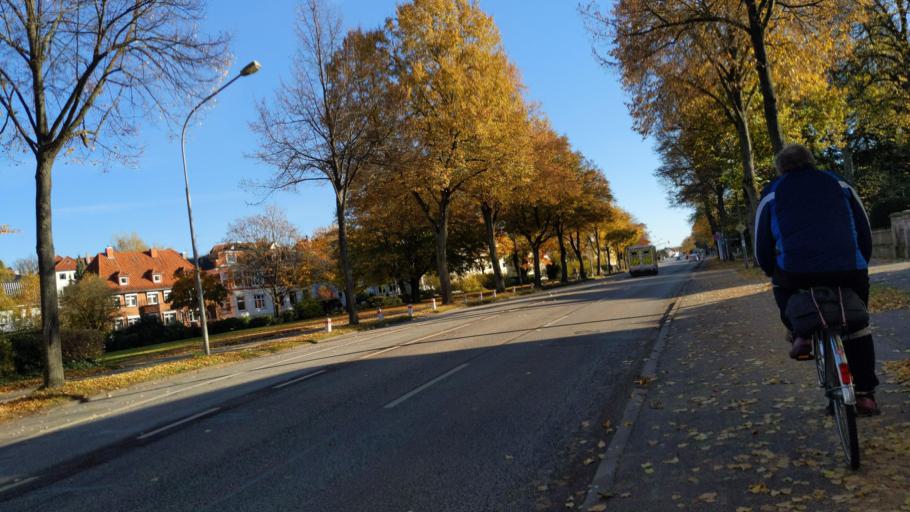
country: DE
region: Schleswig-Holstein
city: Luebeck
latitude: 53.8563
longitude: 10.6937
